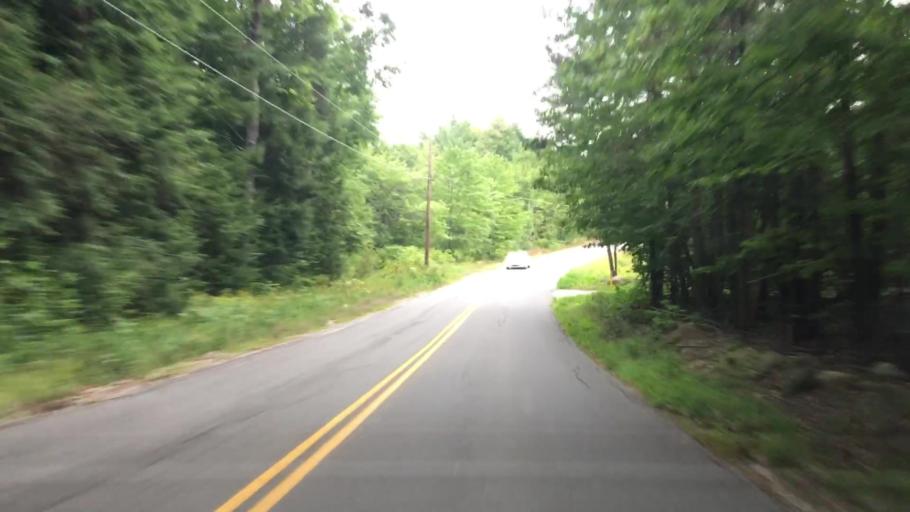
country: US
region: Maine
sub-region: Cumberland County
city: New Gloucester
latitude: 43.9037
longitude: -70.2106
